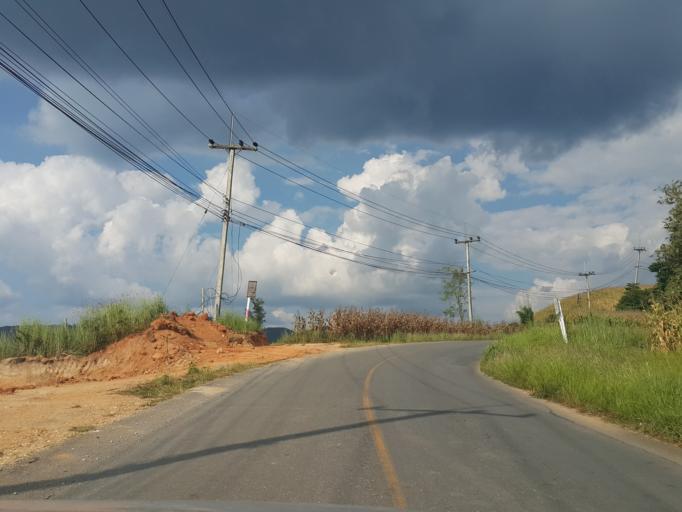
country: TH
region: Chiang Mai
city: Mae Chaem
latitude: 18.5257
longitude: 98.3637
